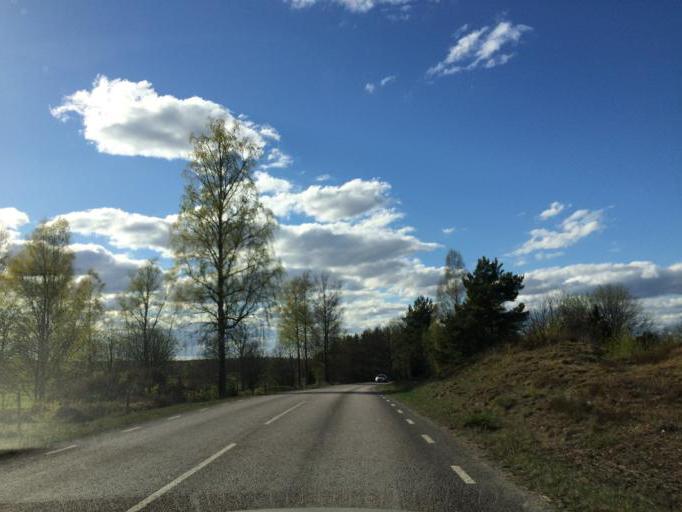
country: SE
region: Soedermanland
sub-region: Eskilstuna Kommun
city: Kvicksund
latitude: 59.4108
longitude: 16.3550
